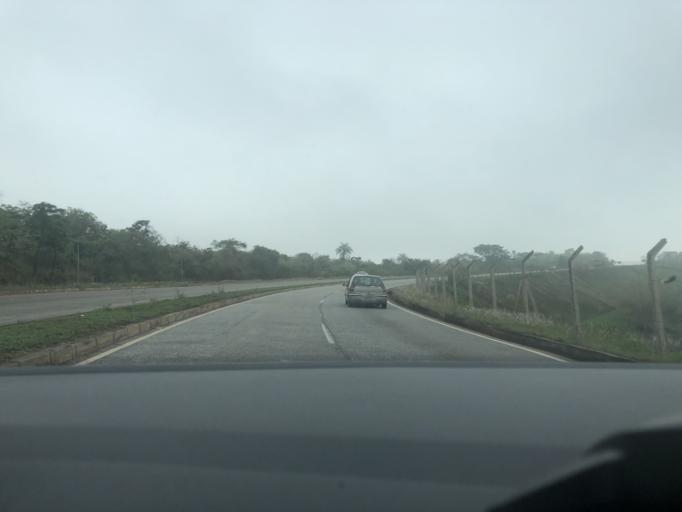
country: BR
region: Minas Gerais
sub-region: Congonhas
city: Congonhas
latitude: -20.5947
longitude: -43.9487
